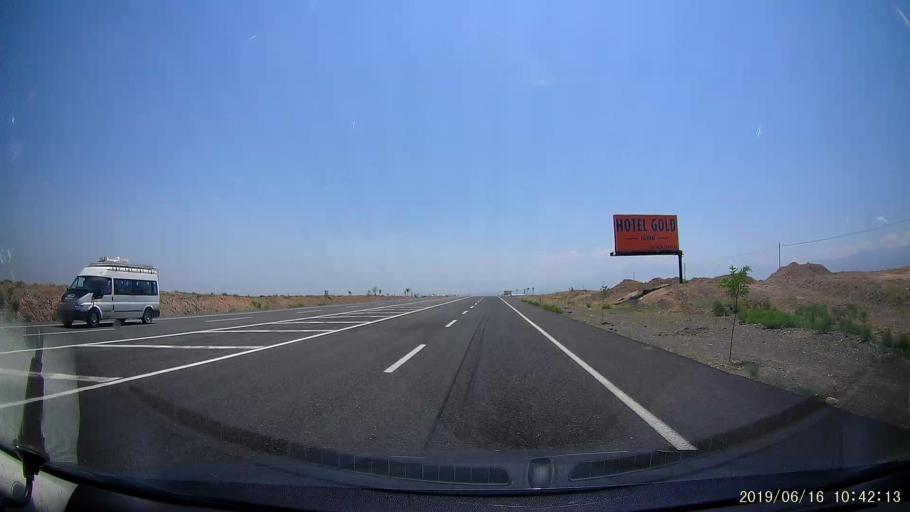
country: AM
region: Armavir
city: Shenavan
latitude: 40.0436
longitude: 43.8018
